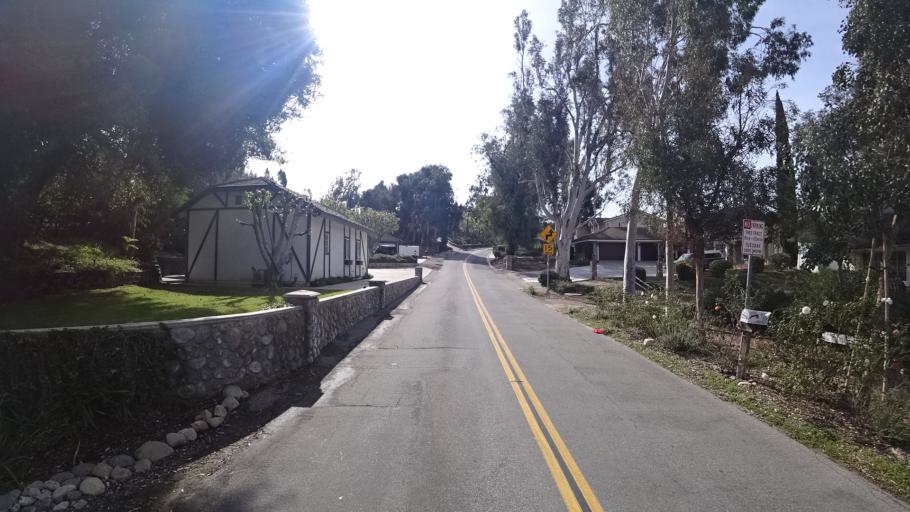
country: US
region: California
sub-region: Orange County
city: Yorba Linda
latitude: 33.8585
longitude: -117.7644
